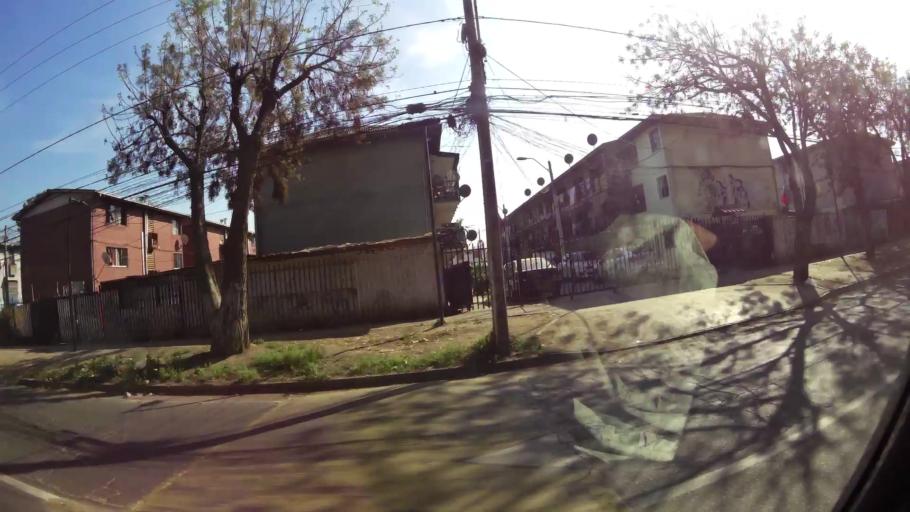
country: CL
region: Santiago Metropolitan
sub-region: Provincia de Santiago
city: Lo Prado
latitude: -33.4659
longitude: -70.7509
